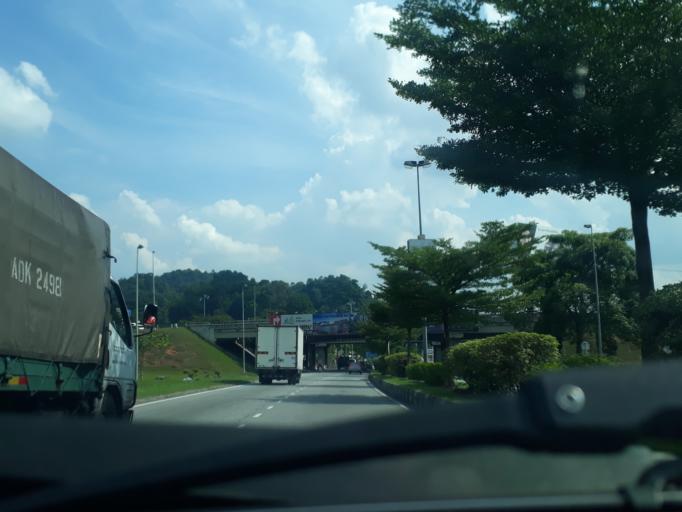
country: MY
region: Perak
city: Ipoh
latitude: 4.6373
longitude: 101.0916
